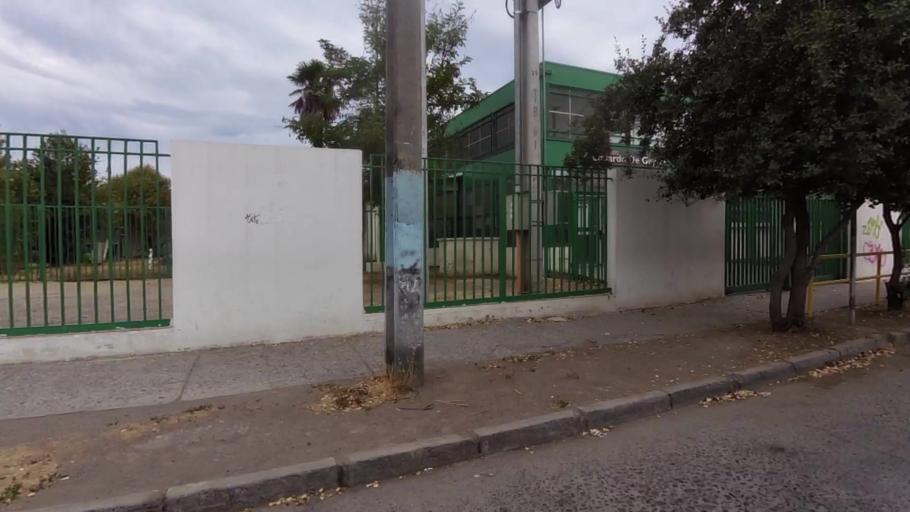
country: CL
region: O'Higgins
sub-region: Provincia de Cachapoal
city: Rancagua
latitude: -34.1611
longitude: -70.7410
